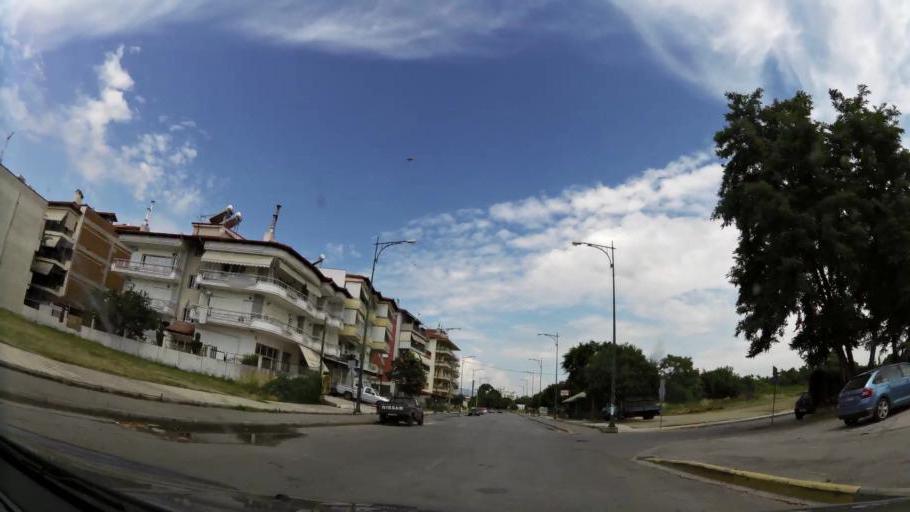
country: GR
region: Central Macedonia
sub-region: Nomos Pierias
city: Katerini
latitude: 40.2758
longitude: 22.5107
